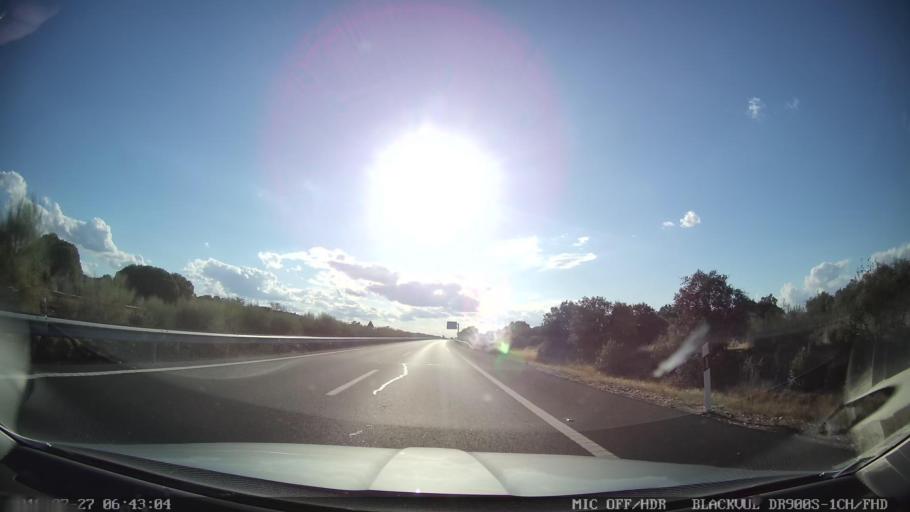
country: ES
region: Extremadura
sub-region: Provincia de Caceres
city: Navalmoral de la Mata
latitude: 39.8889
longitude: -5.4982
